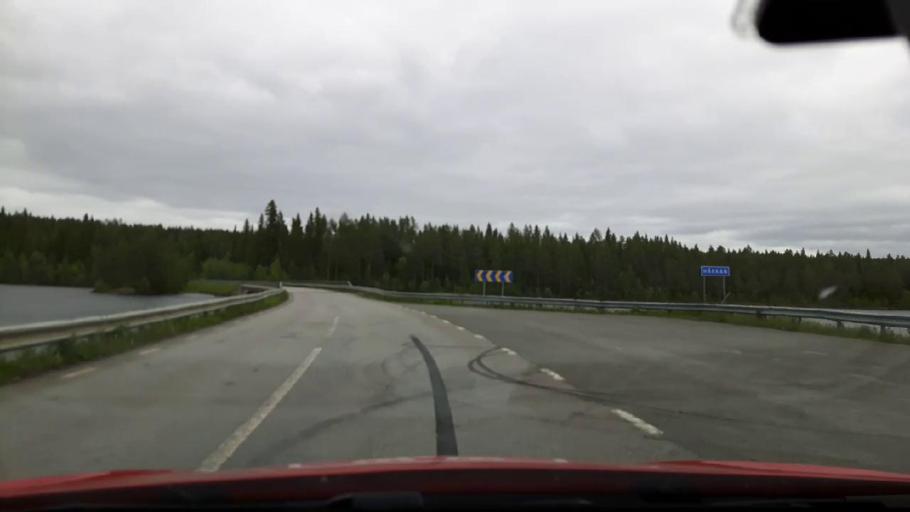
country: SE
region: Jaemtland
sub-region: OEstersunds Kommun
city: Lit
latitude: 63.6735
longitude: 14.6780
